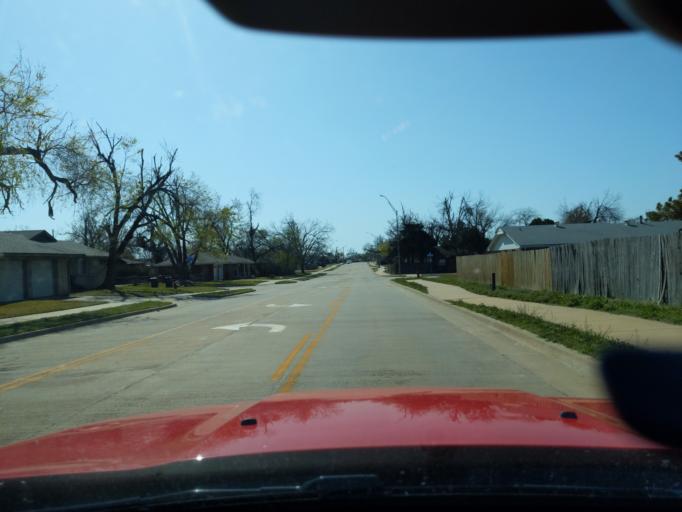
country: US
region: Oklahoma
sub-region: Cleveland County
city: Moore
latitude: 35.3465
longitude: -97.4891
